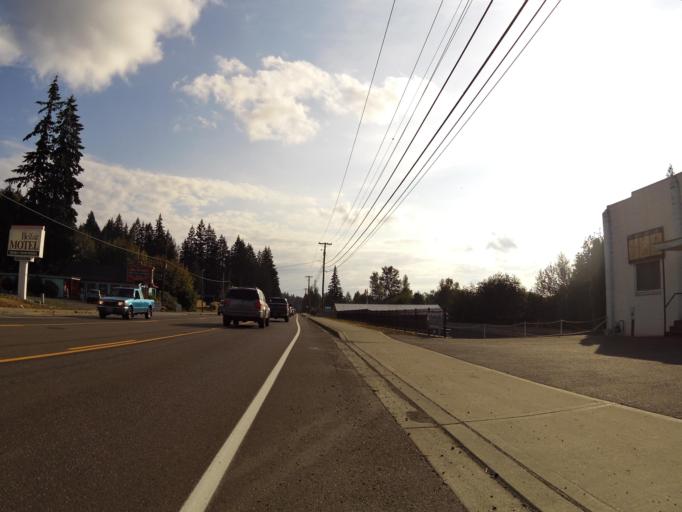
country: US
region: Washington
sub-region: Mason County
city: Belfair
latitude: 47.4458
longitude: -122.8308
